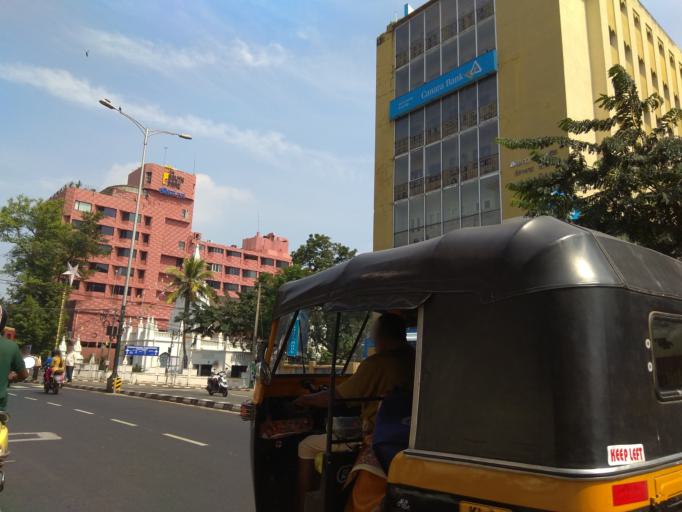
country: IN
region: Kerala
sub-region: Thiruvananthapuram
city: Thiruvananthapuram
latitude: 8.5002
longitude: 76.9491
